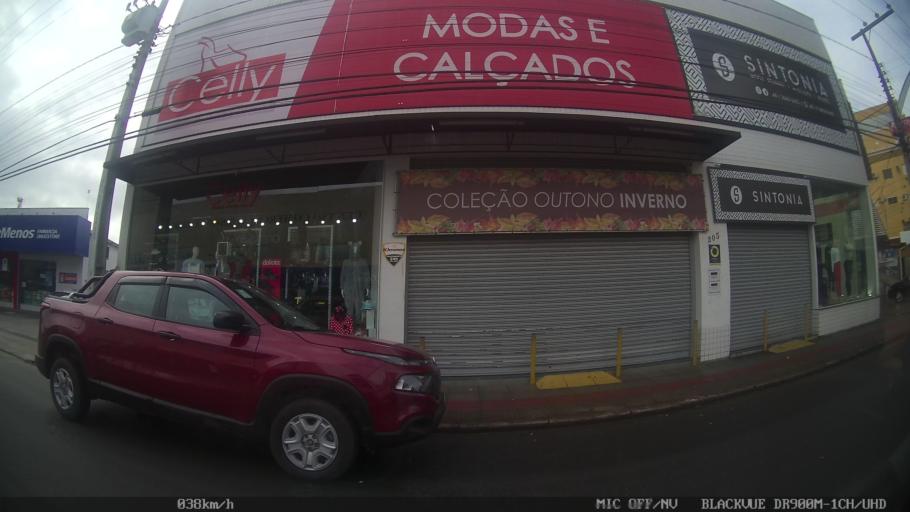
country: BR
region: Santa Catarina
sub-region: Biguacu
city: Biguacu
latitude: -27.4983
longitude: -48.6548
